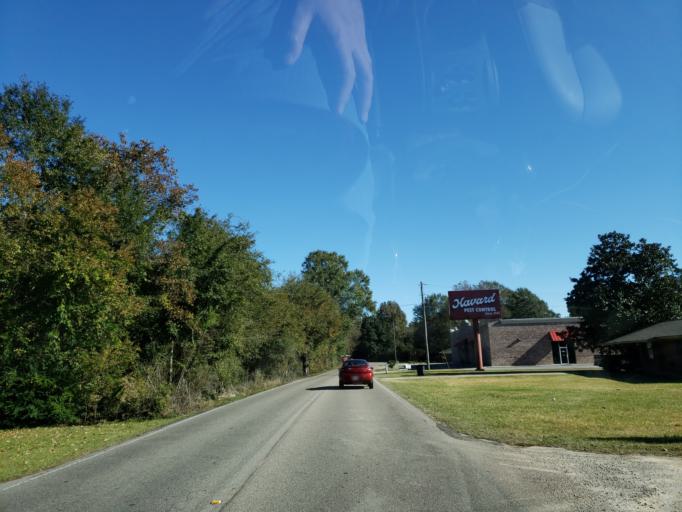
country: US
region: Mississippi
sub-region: Lamar County
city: West Hattiesburg
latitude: 31.3072
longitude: -89.3892
